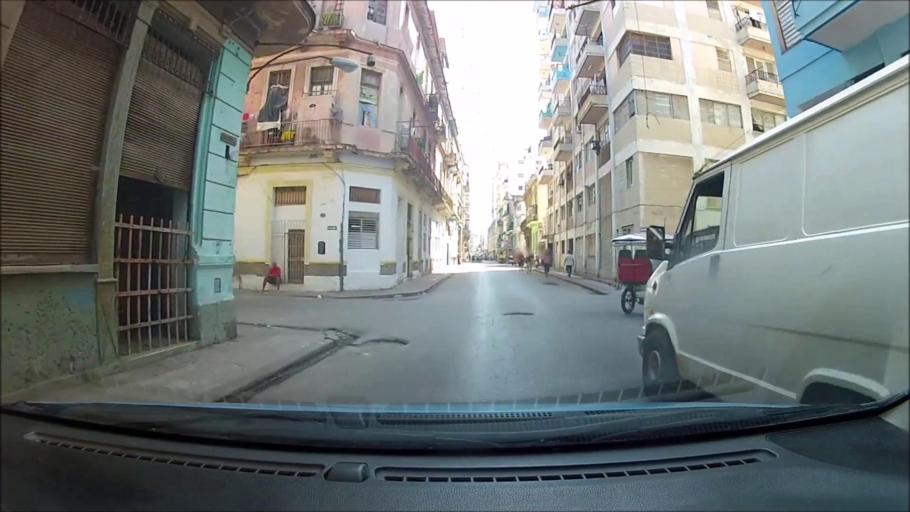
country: CU
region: La Habana
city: Centro Habana
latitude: 23.1392
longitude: -82.3681
